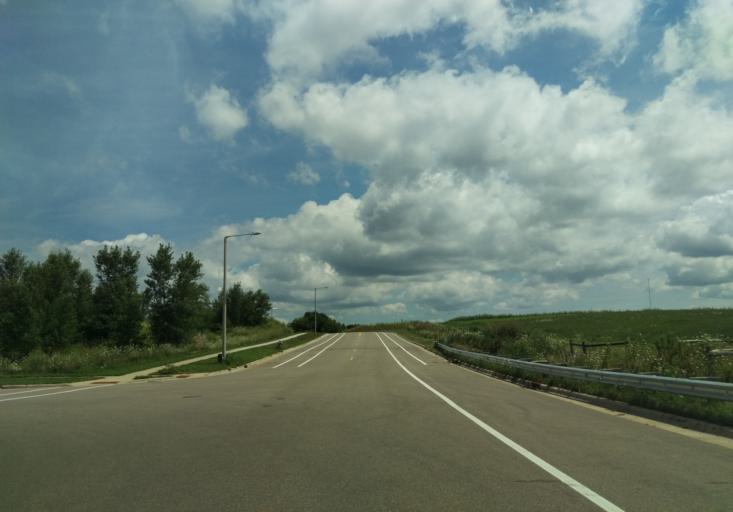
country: US
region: Wisconsin
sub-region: Dane County
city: Middleton
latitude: 43.0677
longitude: -89.5357
